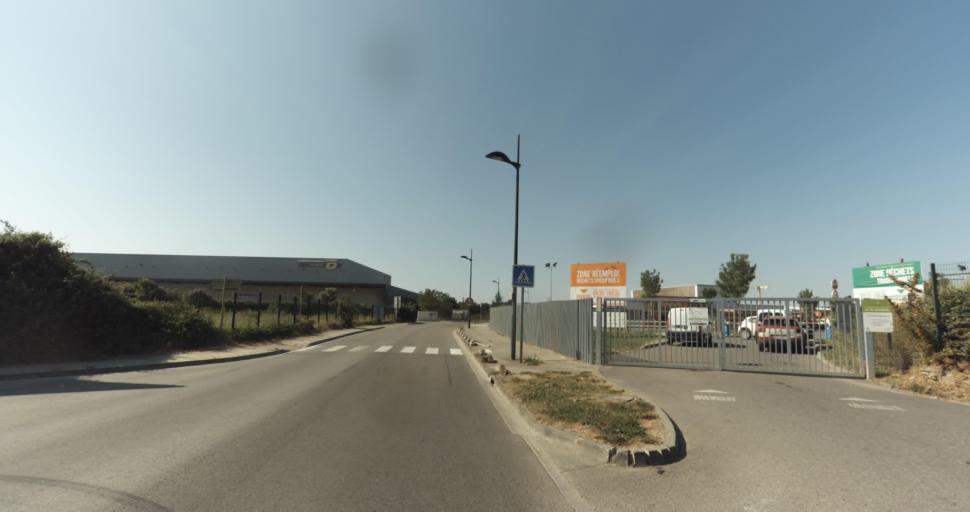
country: FR
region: Midi-Pyrenees
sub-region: Departement de la Haute-Garonne
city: Tournefeuille
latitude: 43.5944
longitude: 1.3005
